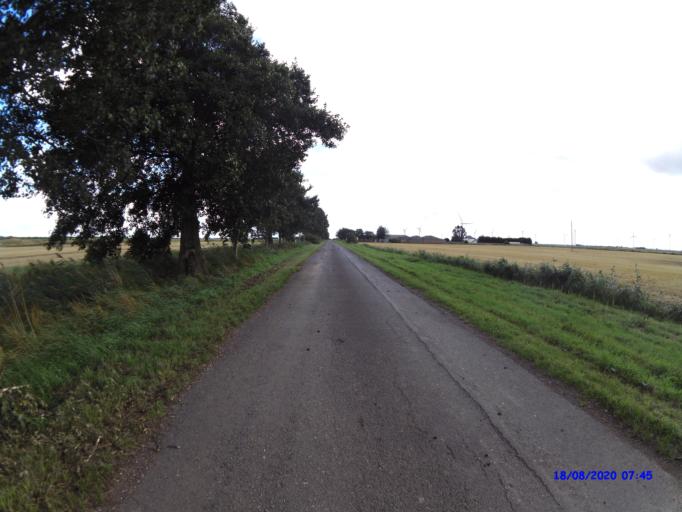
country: GB
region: England
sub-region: Cambridgeshire
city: Whittlesey
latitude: 52.5264
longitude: -0.1029
